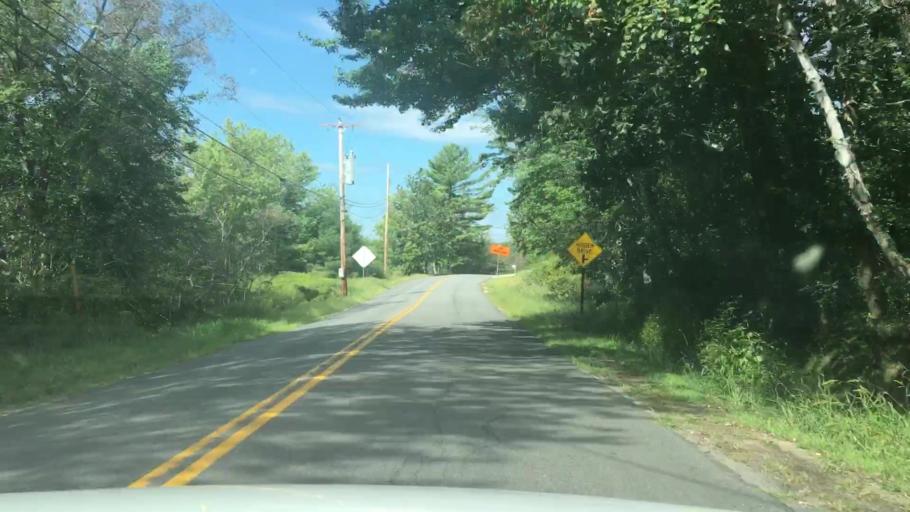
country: US
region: Maine
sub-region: Androscoggin County
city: Auburn
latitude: 44.1565
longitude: -70.2349
